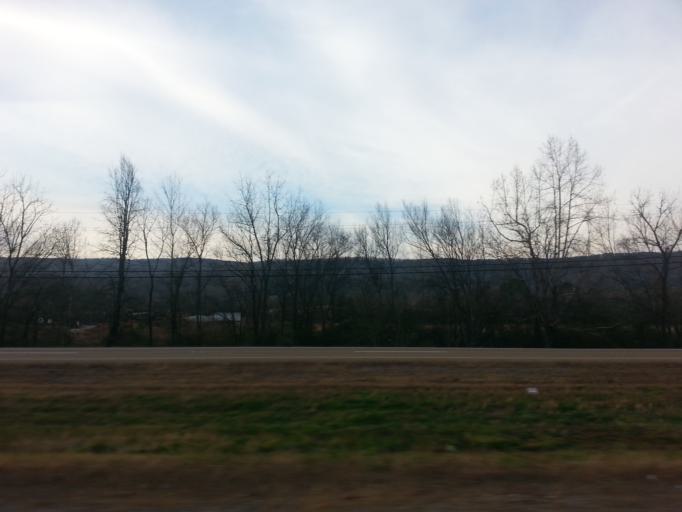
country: US
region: Tennessee
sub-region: Rhea County
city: Dayton
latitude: 35.5455
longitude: -84.9686
